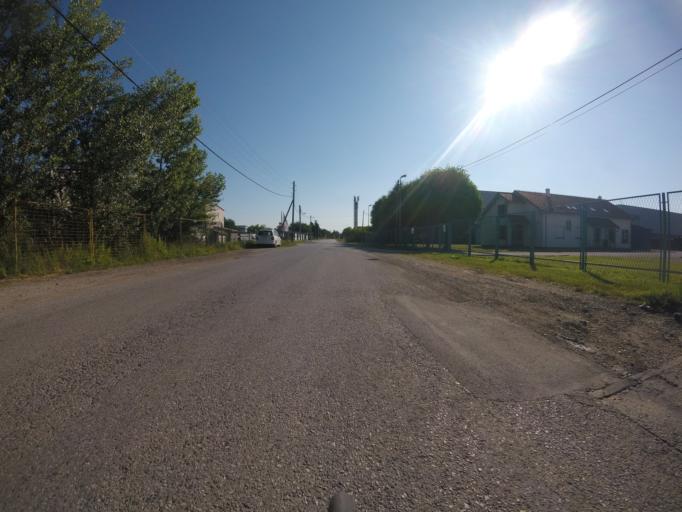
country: HR
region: Grad Zagreb
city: Lucko
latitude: 45.7544
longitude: 15.8774
